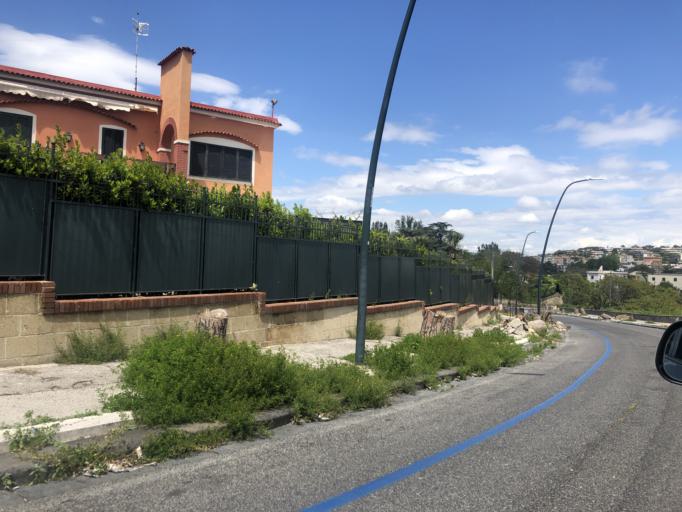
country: IT
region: Campania
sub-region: Provincia di Napoli
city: Bagnoli
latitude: 40.7980
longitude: 14.1825
